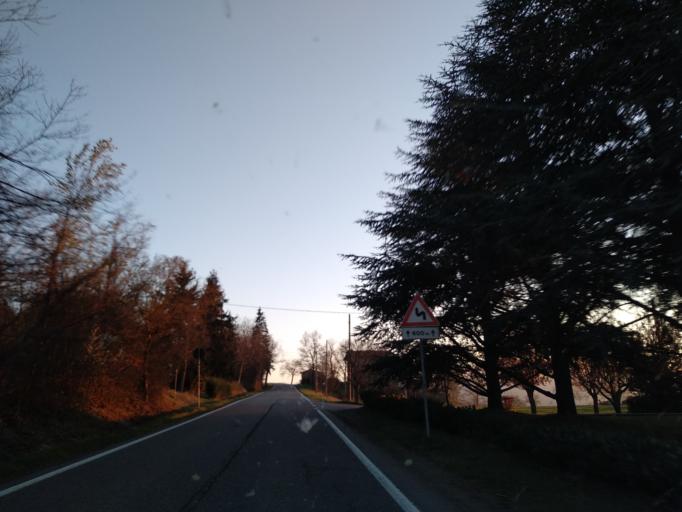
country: IT
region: Emilia-Romagna
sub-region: Provincia di Reggio Emilia
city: Castelnovo ne'Monti
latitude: 44.4258
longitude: 10.4066
